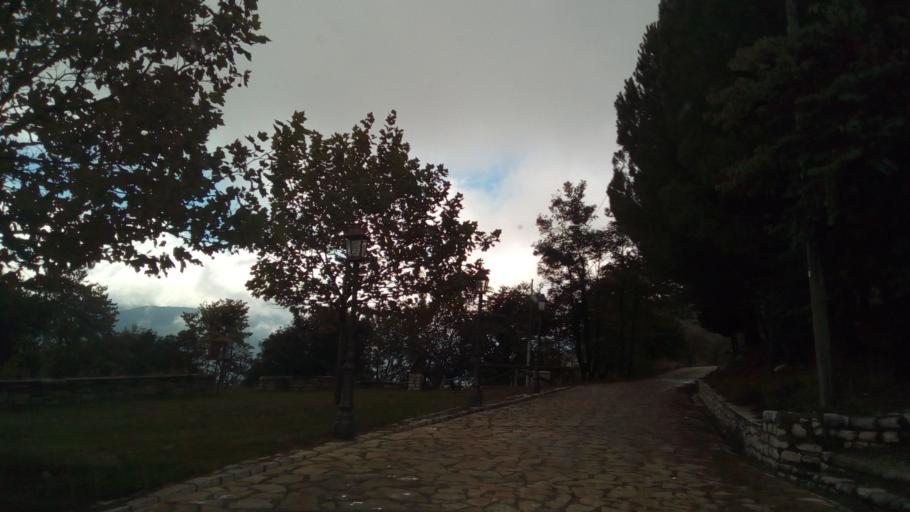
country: GR
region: West Greece
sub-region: Nomos Aitolias kai Akarnanias
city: Thermo
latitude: 38.5949
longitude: 21.7938
